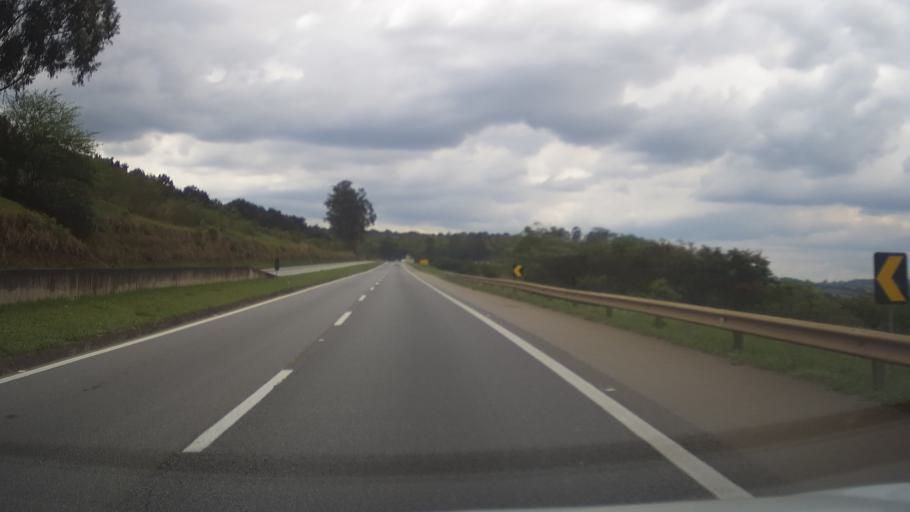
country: BR
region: Minas Gerais
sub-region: Tres Coracoes
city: Tres Coracoes
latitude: -21.5085
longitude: -45.2152
